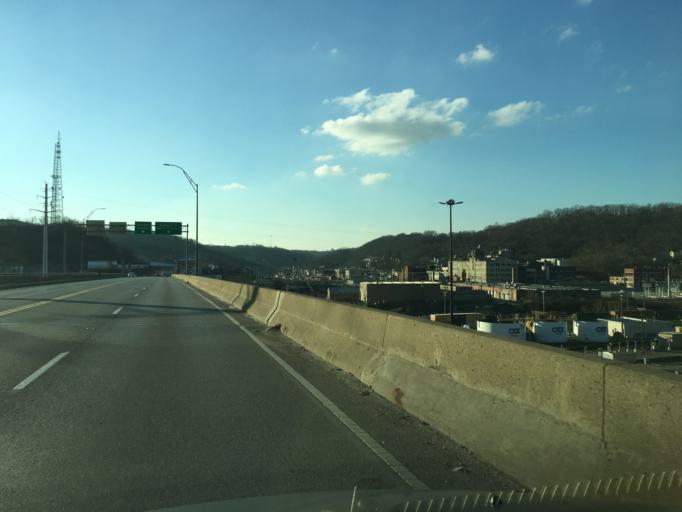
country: US
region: Kentucky
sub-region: Kenton County
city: Ludlow
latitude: 39.1249
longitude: -84.5398
